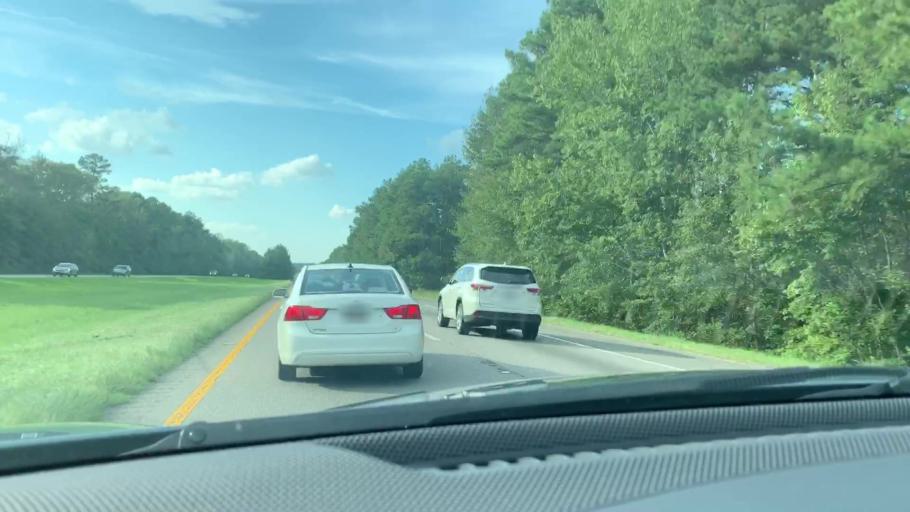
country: US
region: South Carolina
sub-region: Orangeburg County
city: Brookdale
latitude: 33.4424
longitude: -80.7092
